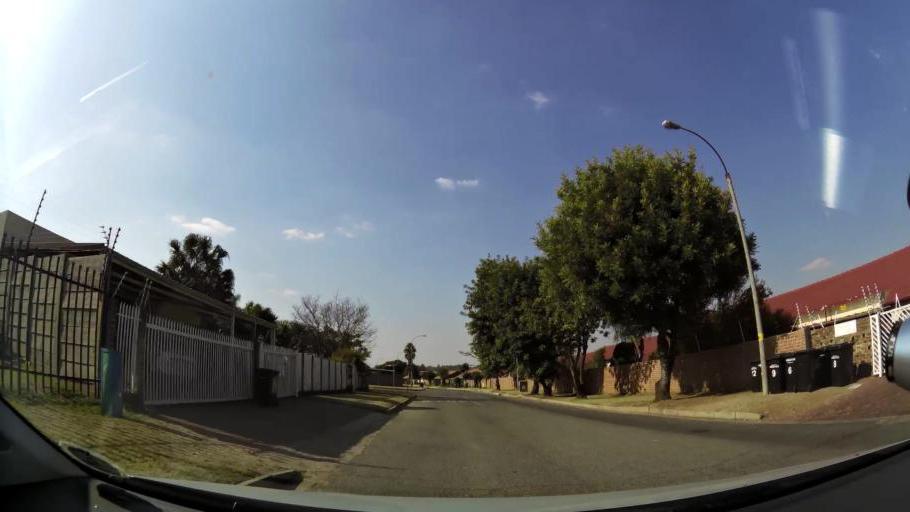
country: ZA
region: Gauteng
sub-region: City of Johannesburg Metropolitan Municipality
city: Modderfontein
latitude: -26.0981
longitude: 28.2123
